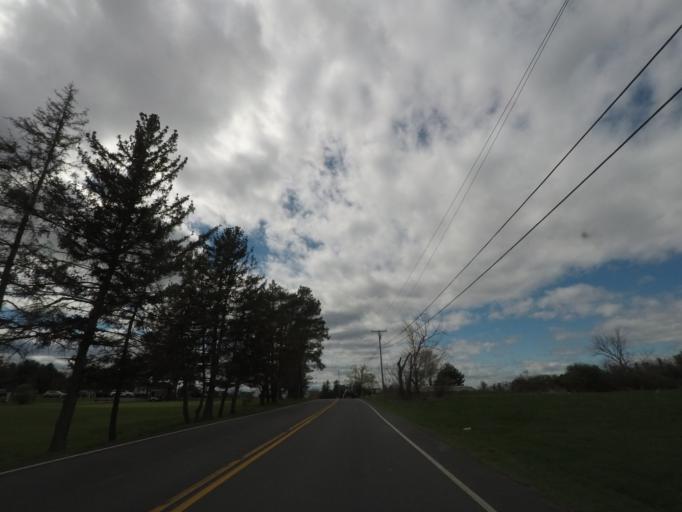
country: US
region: New York
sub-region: Columbia County
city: Valatie
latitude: 42.3995
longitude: -73.6614
